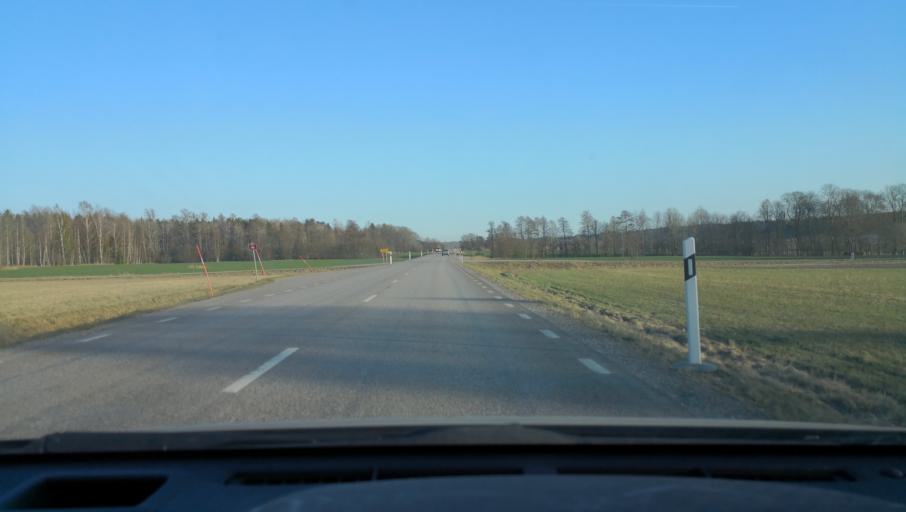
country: SE
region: Uppsala
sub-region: Heby Kommun
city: Heby
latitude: 59.9037
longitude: 16.8967
